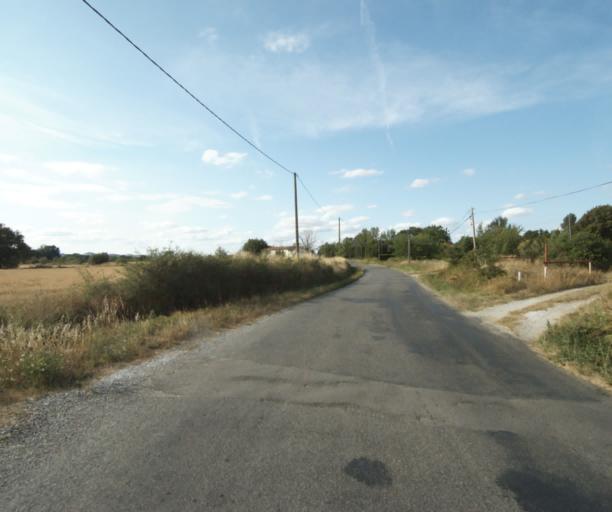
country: FR
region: Midi-Pyrenees
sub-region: Departement de la Haute-Garonne
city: Revel
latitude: 43.4763
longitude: 1.9910
